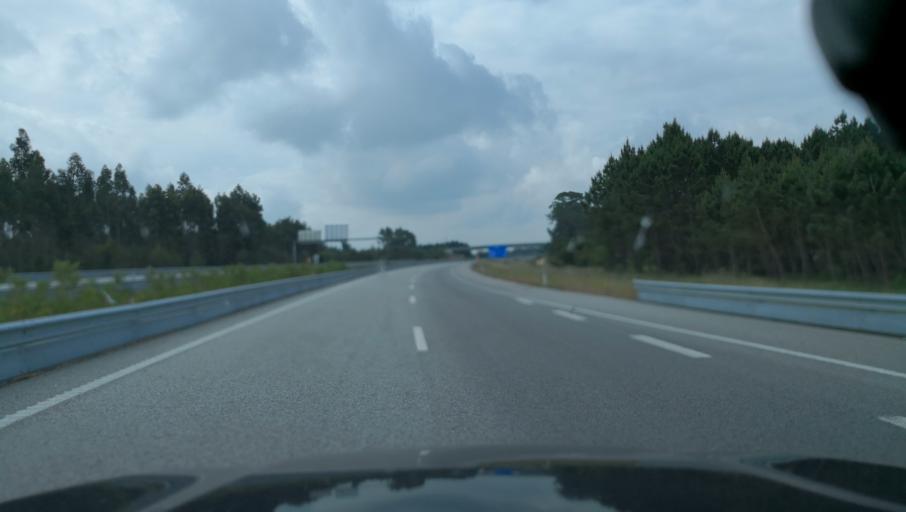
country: PT
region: Coimbra
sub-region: Montemor-O-Velho
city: Arazede
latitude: 40.3225
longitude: -8.7210
